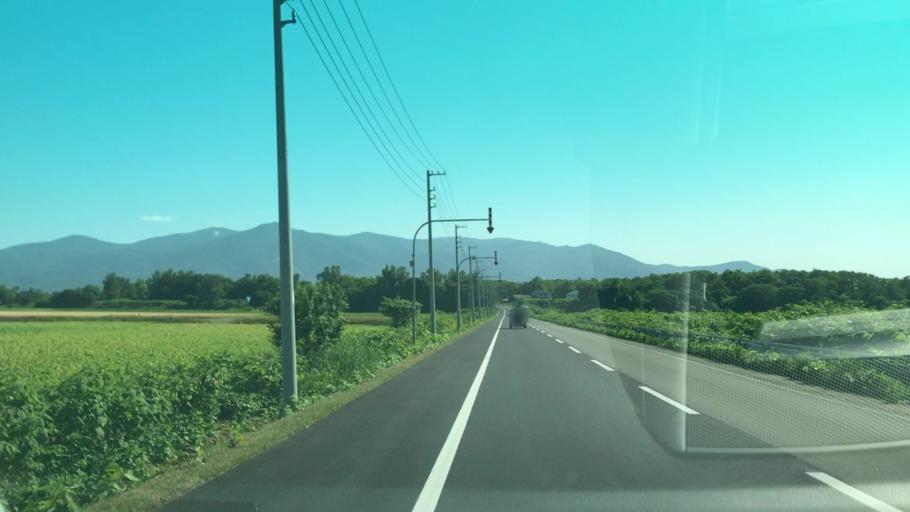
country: JP
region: Hokkaido
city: Iwanai
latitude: 43.0196
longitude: 140.5470
